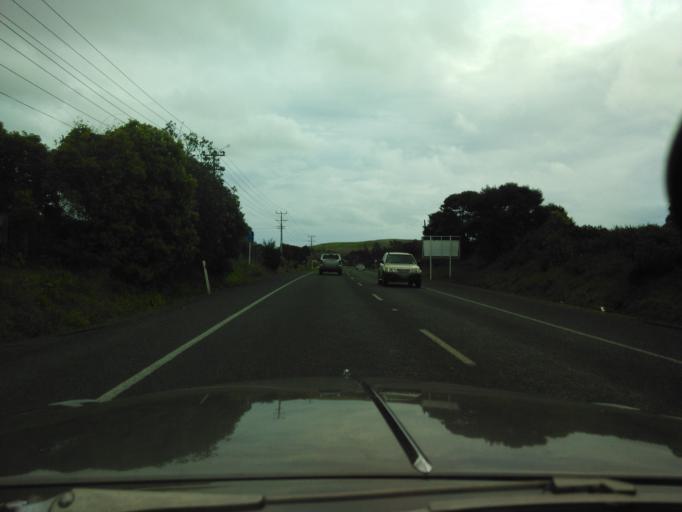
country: NZ
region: Auckland
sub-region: Auckland
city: Muriwai Beach
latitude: -36.7666
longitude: 174.5013
